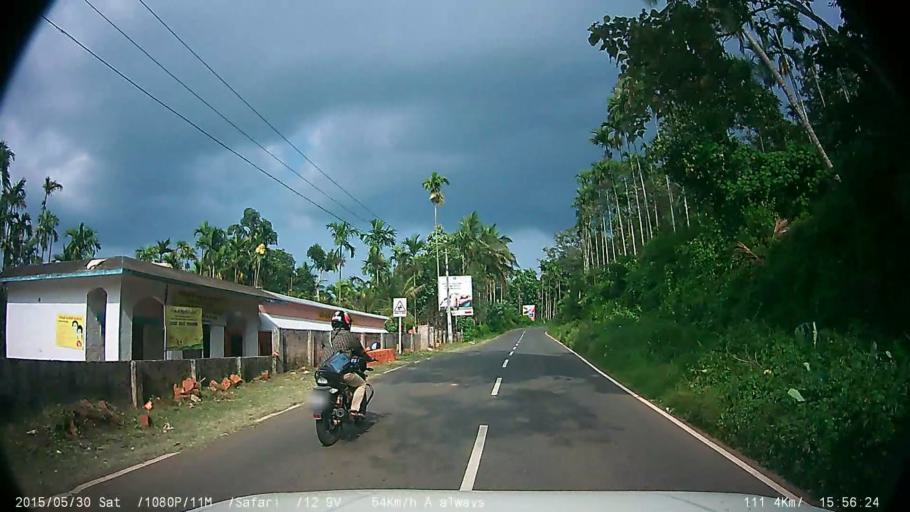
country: IN
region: Kerala
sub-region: Wayanad
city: Kalpetta
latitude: 11.6596
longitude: 76.0846
